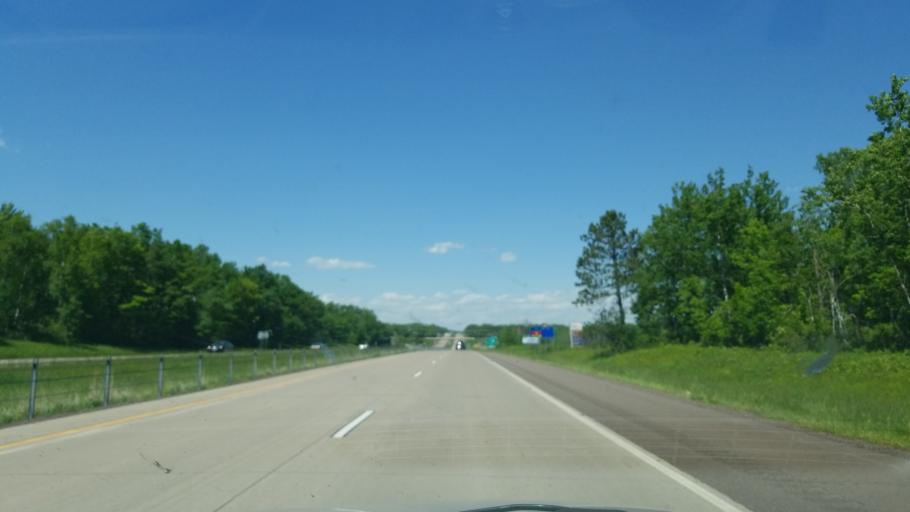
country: US
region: Minnesota
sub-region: Pine County
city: Sandstone
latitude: 46.1176
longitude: -92.8878
